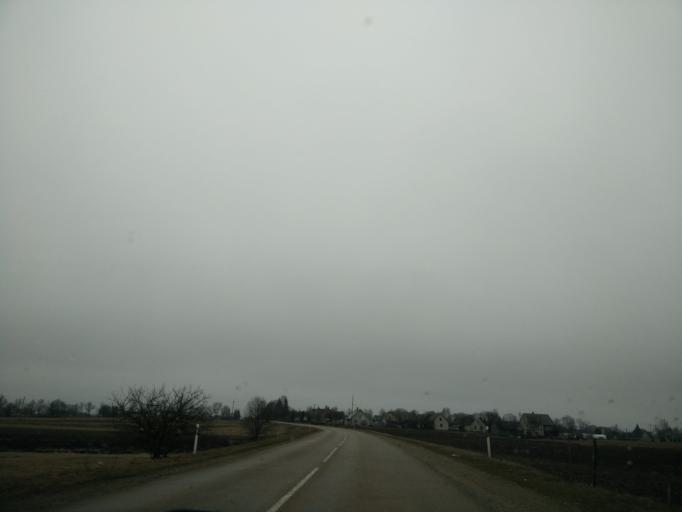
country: LT
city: Ariogala
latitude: 55.3238
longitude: 23.4264
